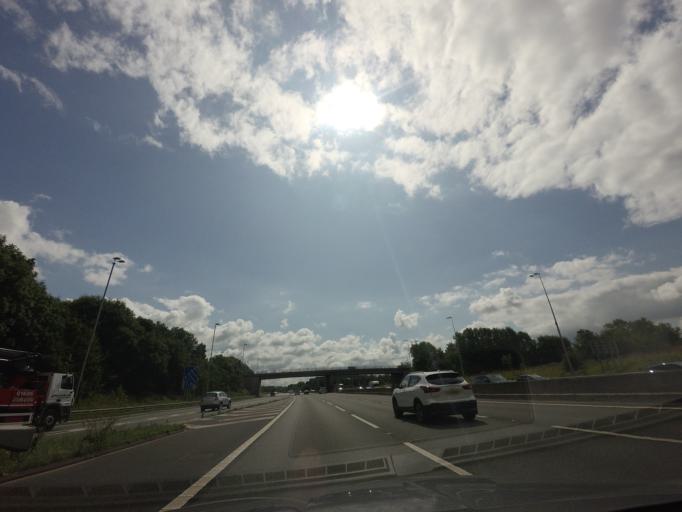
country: GB
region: England
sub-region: Lancashire
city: Goosnargh
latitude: 53.8029
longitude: -2.6934
